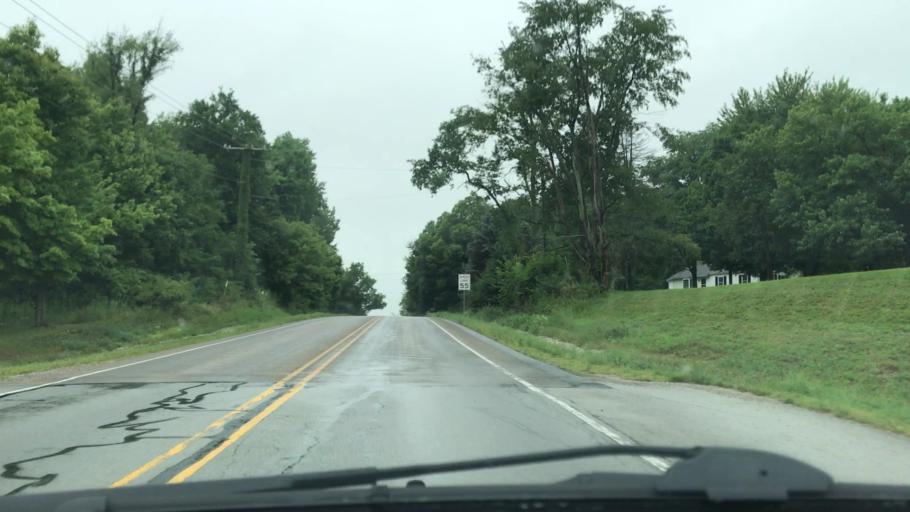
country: US
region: Indiana
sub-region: Hamilton County
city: Westfield
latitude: 40.0962
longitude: -86.1320
